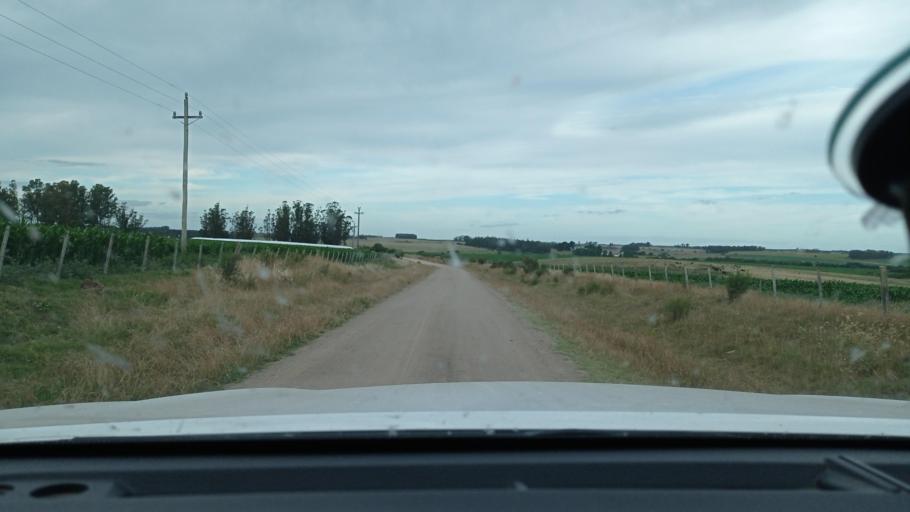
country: UY
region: Florida
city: Casupa
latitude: -34.1029
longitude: -55.7506
